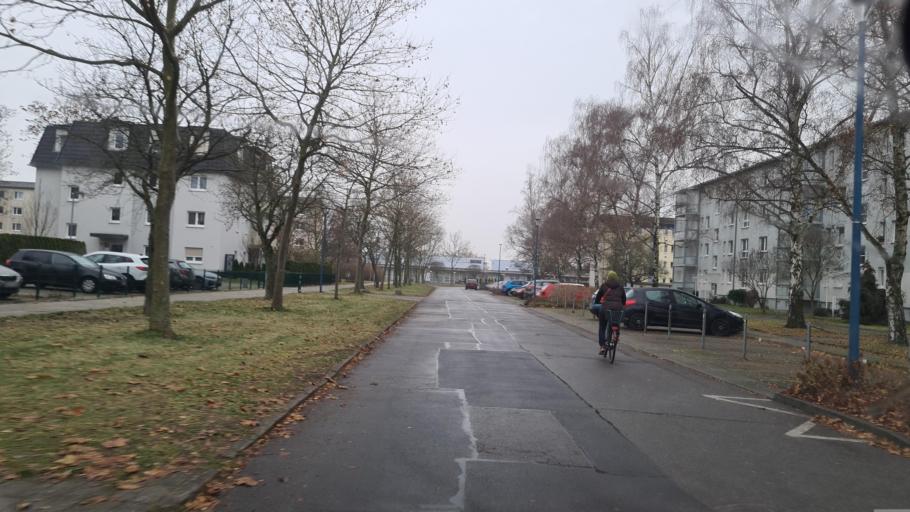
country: DE
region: Brandenburg
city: Cottbus
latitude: 51.7457
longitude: 14.3199
